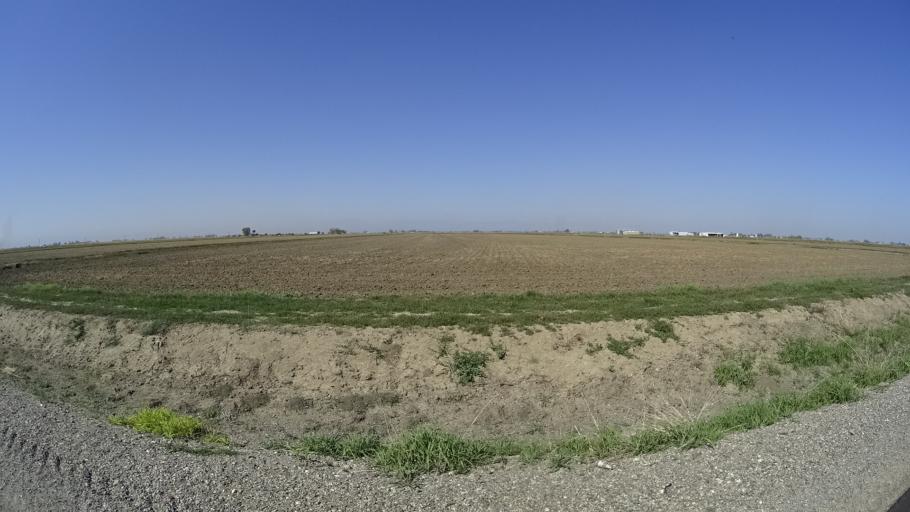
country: US
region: California
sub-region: Glenn County
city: Willows
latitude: 39.5250
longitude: -122.0653
